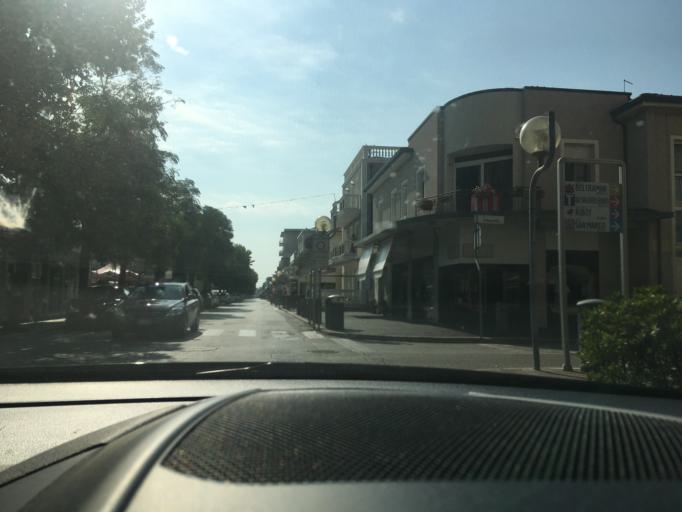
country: IT
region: Emilia-Romagna
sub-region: Provincia di Rimini
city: Santa Giustina
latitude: 44.1084
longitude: 12.5110
